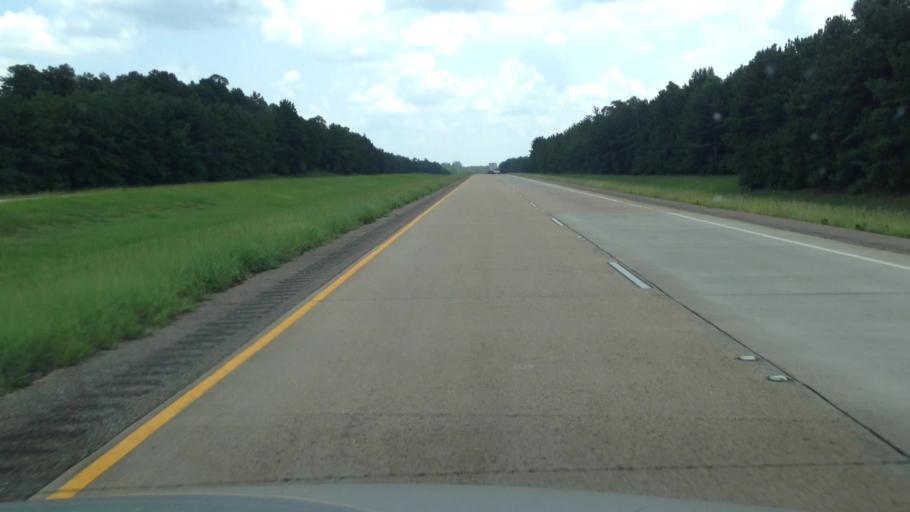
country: US
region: Louisiana
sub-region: Rapides Parish
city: Lecompte
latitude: 31.0526
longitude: -92.4230
